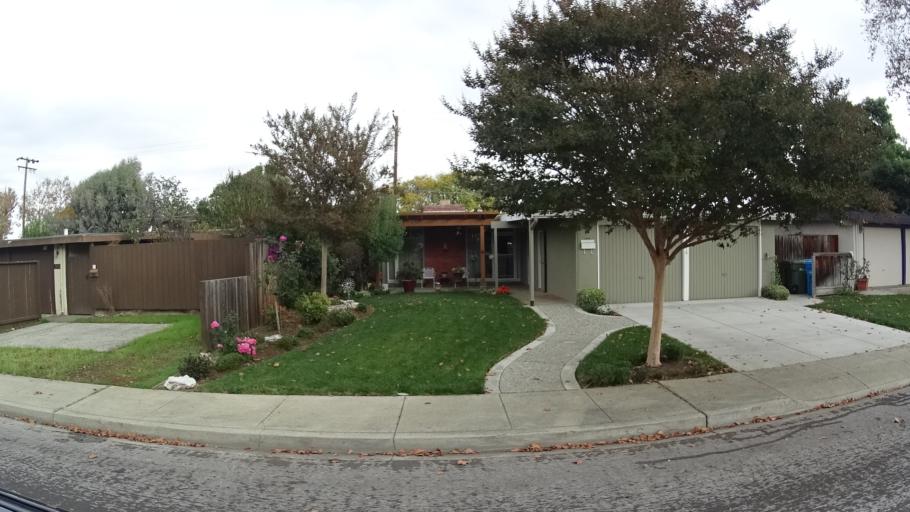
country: US
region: California
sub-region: Santa Clara County
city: Santa Clara
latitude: 37.3266
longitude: -121.9810
